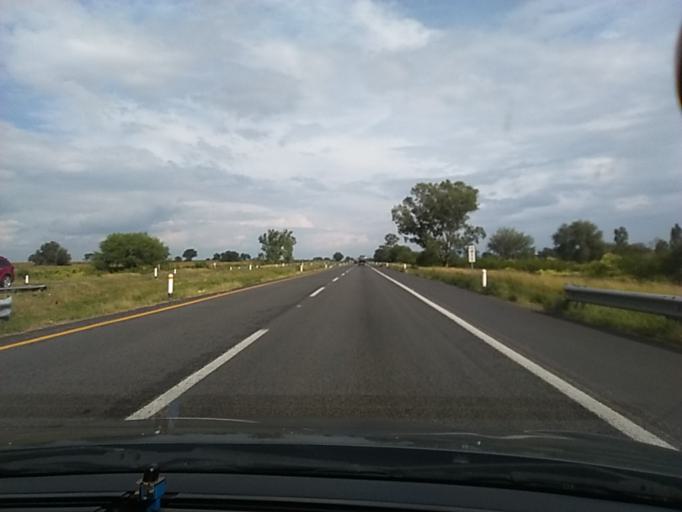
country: MX
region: Jalisco
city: La Barca
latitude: 20.3433
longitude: -102.6161
